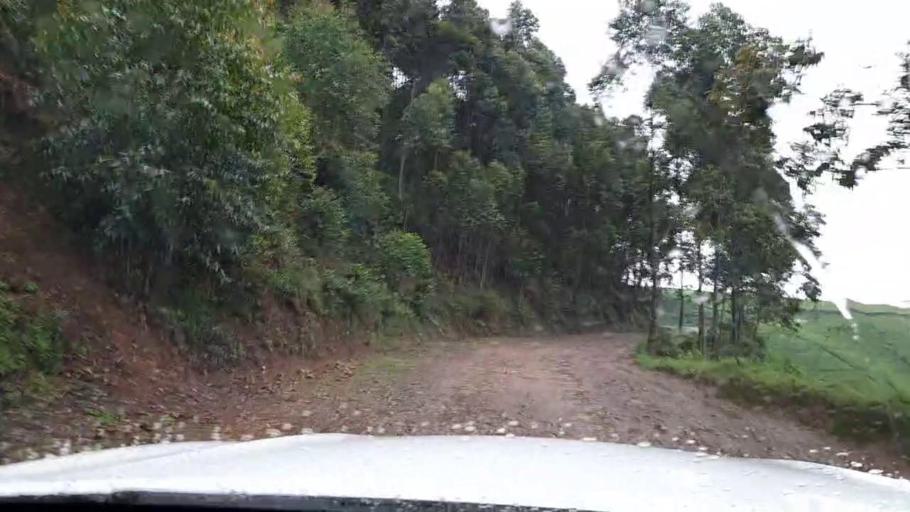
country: RW
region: Western Province
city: Cyangugu
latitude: -2.4597
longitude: 29.0368
